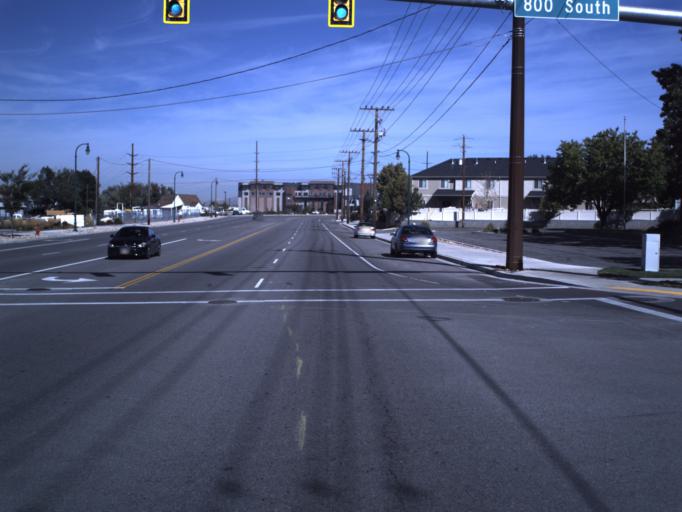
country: US
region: Utah
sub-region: Utah County
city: Orem
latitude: 40.2823
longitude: -111.7320
